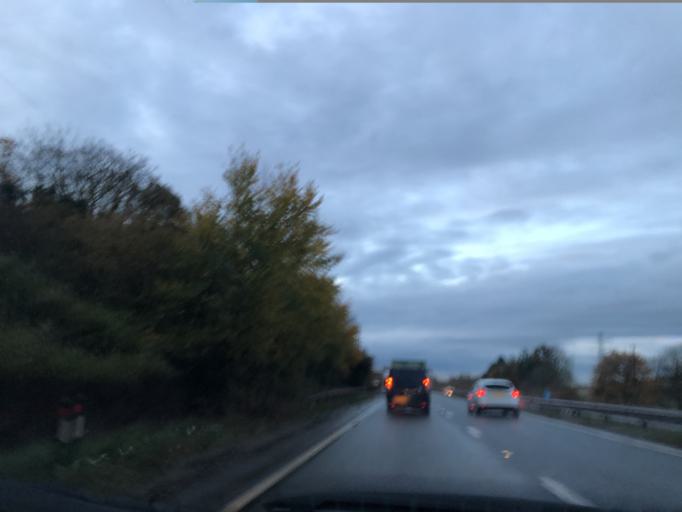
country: GB
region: England
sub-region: Solihull
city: Hampton in Arden
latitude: 52.4539
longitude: -1.6968
